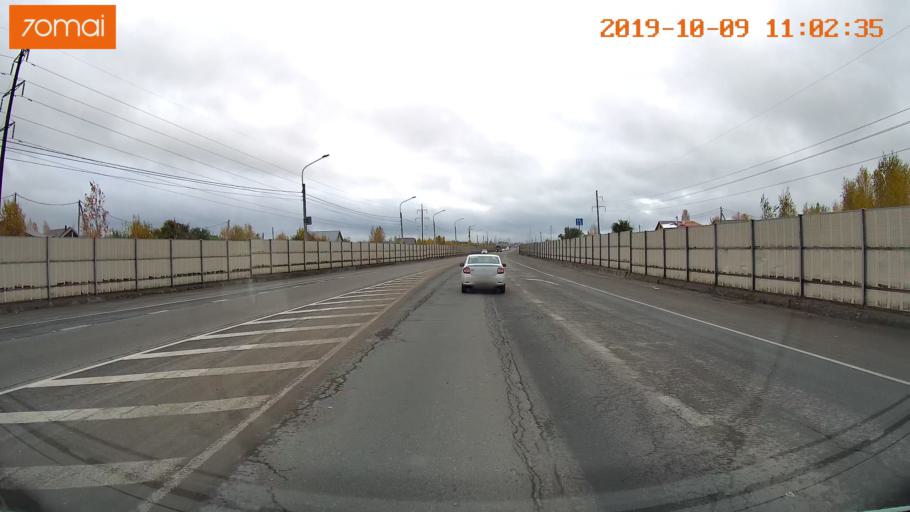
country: RU
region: Vologda
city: Vologda
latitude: 59.2298
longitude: 39.7745
